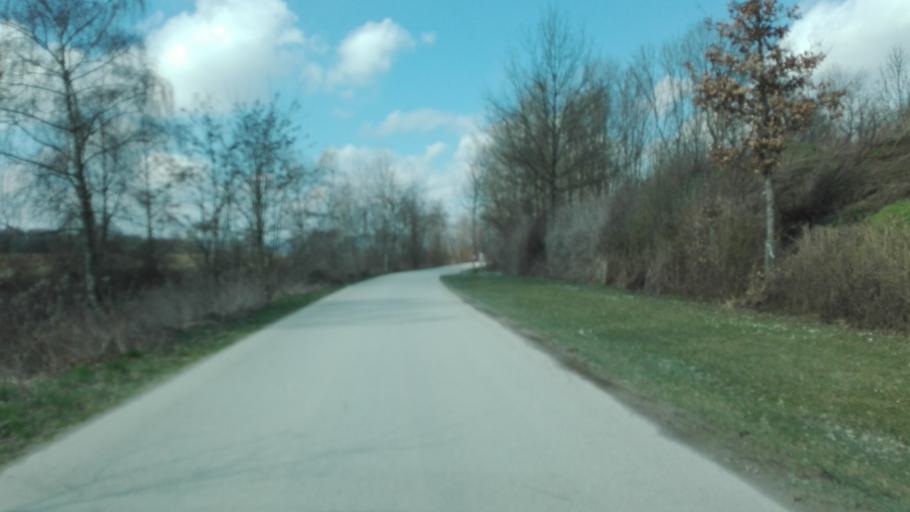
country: AT
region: Upper Austria
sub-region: Politischer Bezirk Urfahr-Umgebung
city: Feldkirchen an der Donau
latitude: 48.3217
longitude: 14.0665
